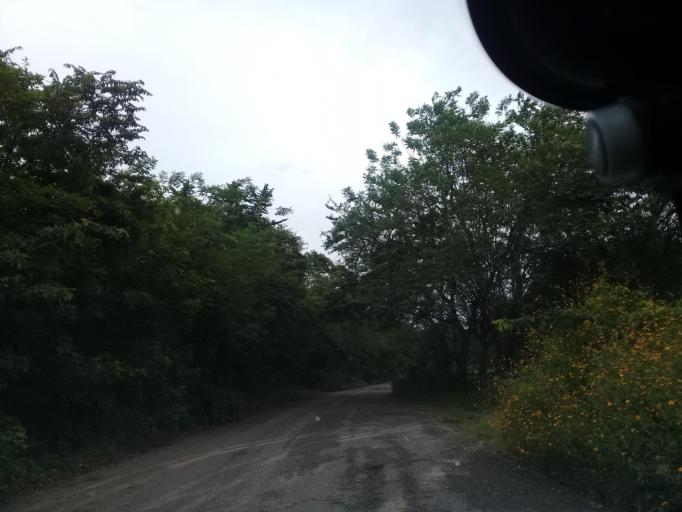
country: MX
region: Hidalgo
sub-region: Huejutla de Reyes
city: Chalahuiyapa
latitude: 21.2003
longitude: -98.3397
